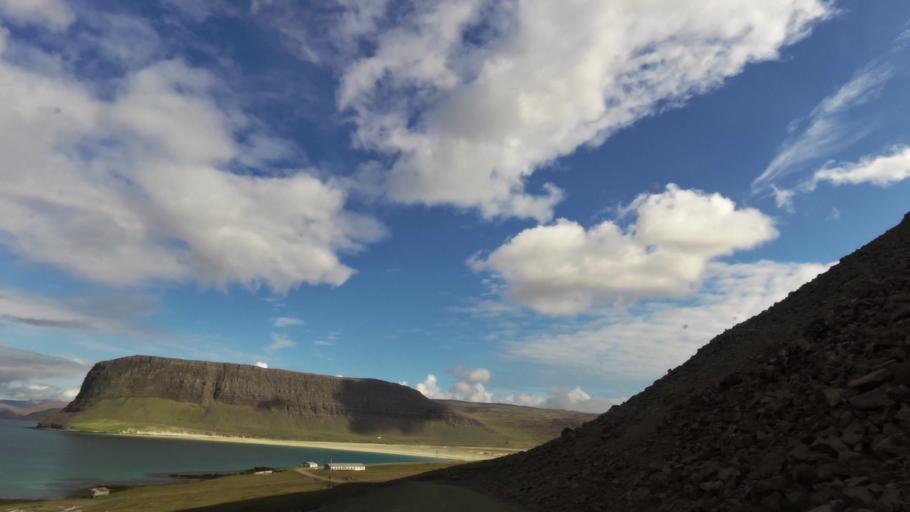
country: IS
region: West
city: Olafsvik
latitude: 65.5947
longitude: -24.1293
